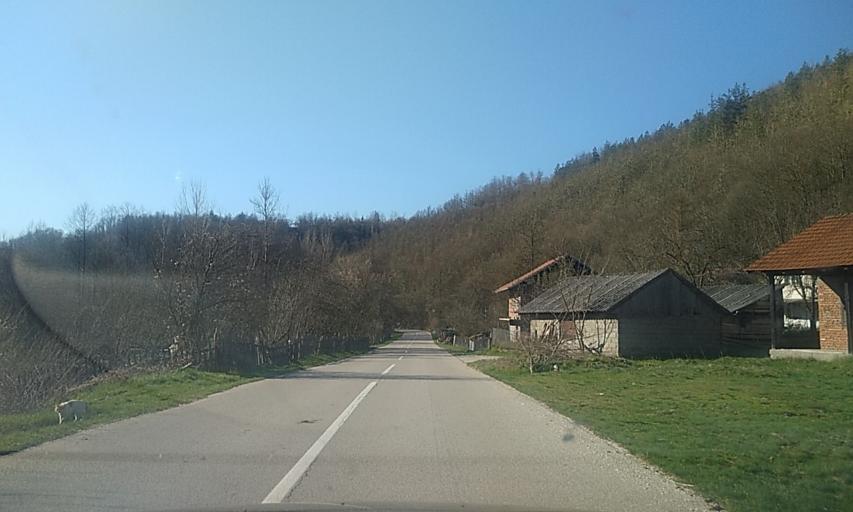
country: RS
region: Central Serbia
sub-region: Pcinjski Okrug
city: Bosilegrad
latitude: 42.4482
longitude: 22.5008
